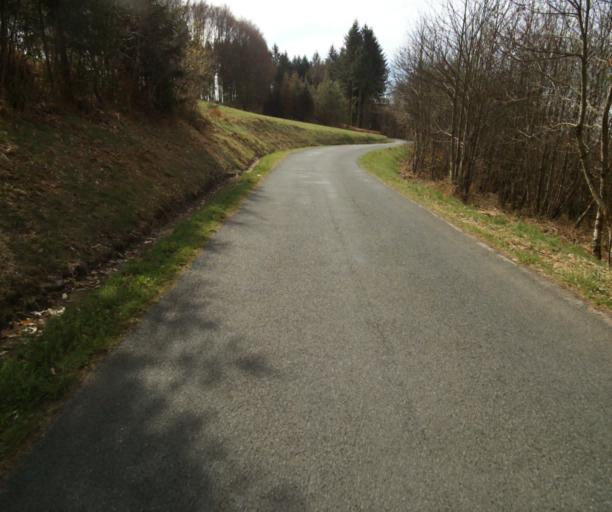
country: FR
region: Limousin
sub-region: Departement de la Correze
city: Correze
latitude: 45.3745
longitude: 1.9020
